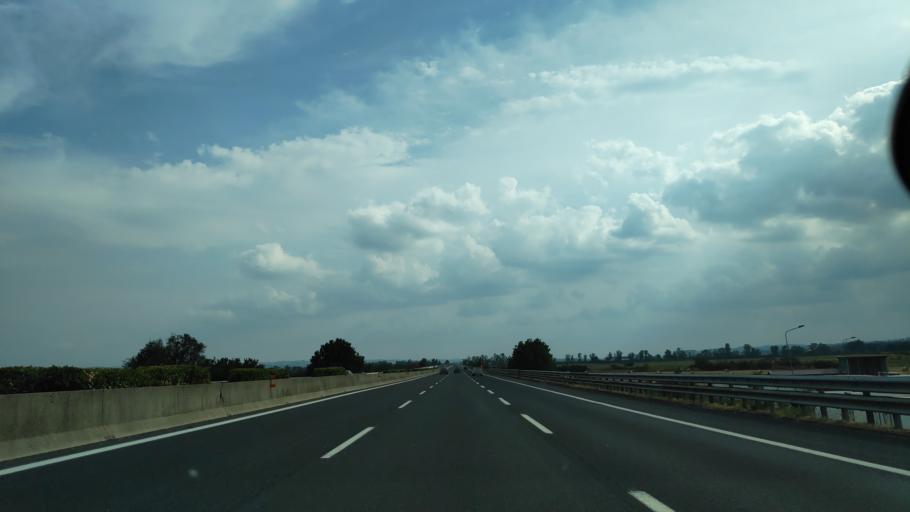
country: IT
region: Latium
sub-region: Citta metropolitana di Roma Capitale
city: Fiano Romano
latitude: 42.1445
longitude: 12.6224
